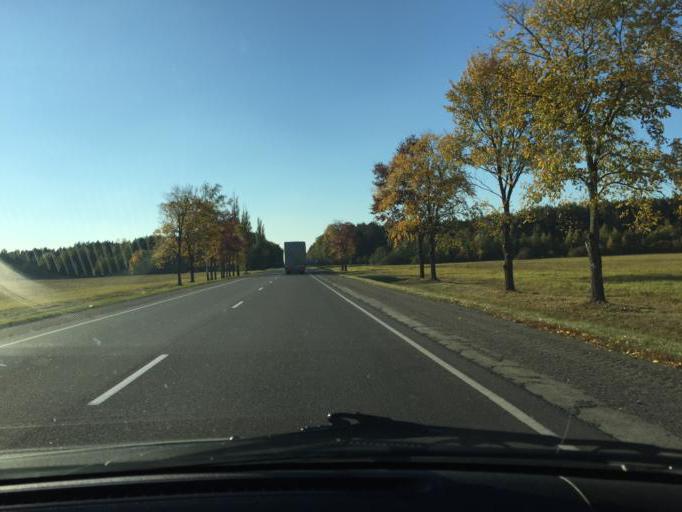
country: BY
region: Brest
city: Luninyets
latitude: 52.2760
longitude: 26.8705
